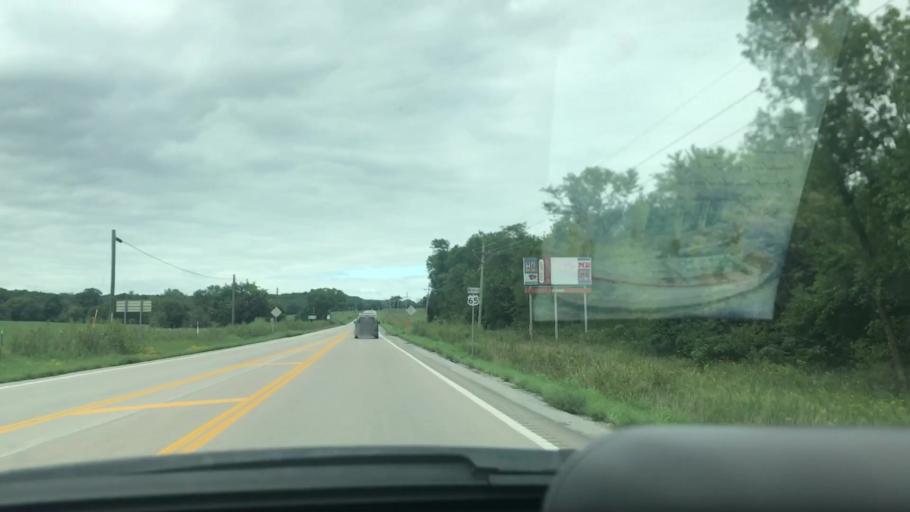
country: US
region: Missouri
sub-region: Hickory County
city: Hermitage
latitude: 37.8610
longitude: -93.1775
